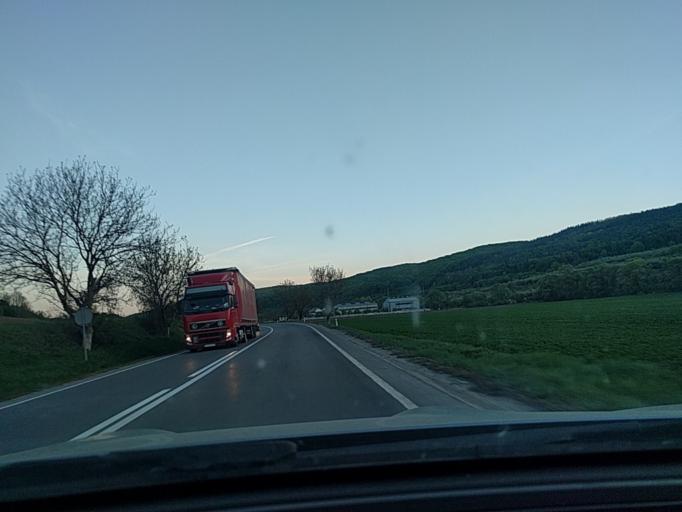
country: RO
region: Mures
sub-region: Comuna Nades
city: Nades
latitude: 46.3349
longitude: 24.7106
